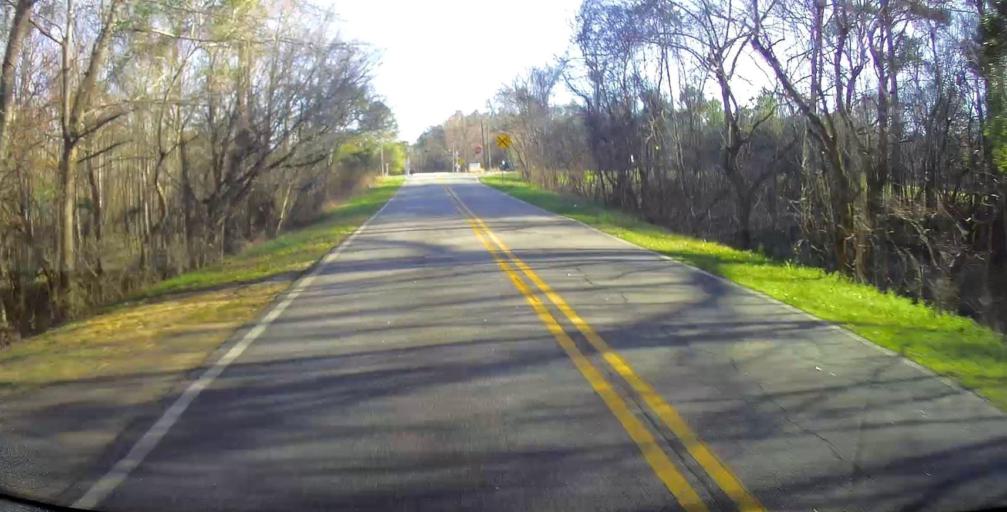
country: US
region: Georgia
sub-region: Muscogee County
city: Columbus
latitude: 32.5513
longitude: -84.7788
